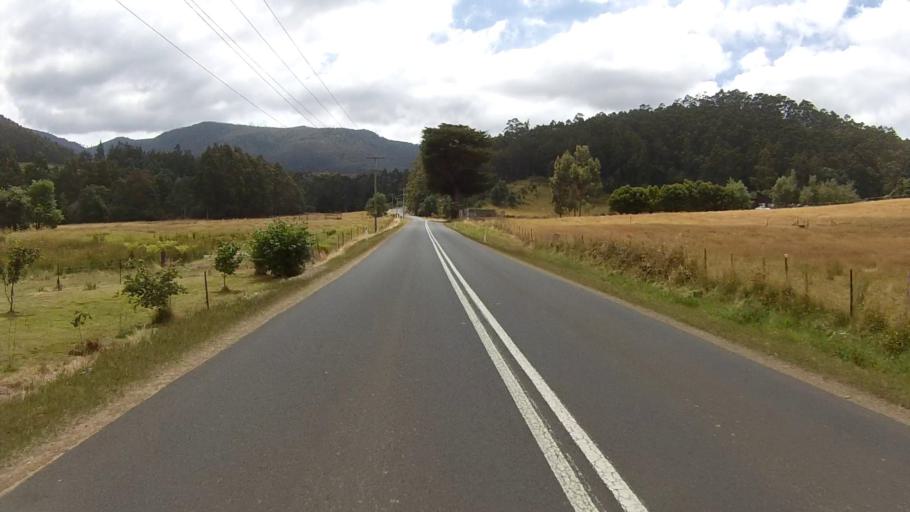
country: AU
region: Tasmania
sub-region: Huon Valley
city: Cygnet
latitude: -43.1349
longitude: 147.1547
